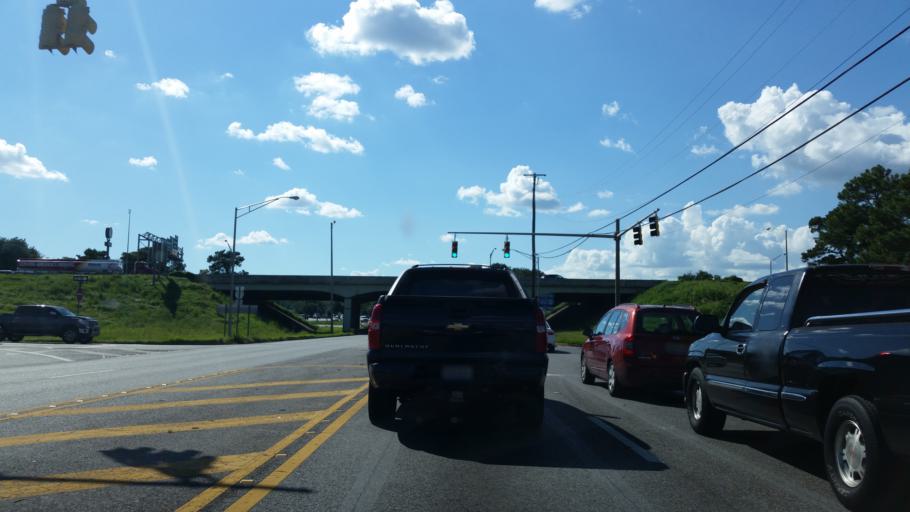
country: US
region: Alabama
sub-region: Mobile County
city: Prichard
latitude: 30.7035
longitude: -88.1220
